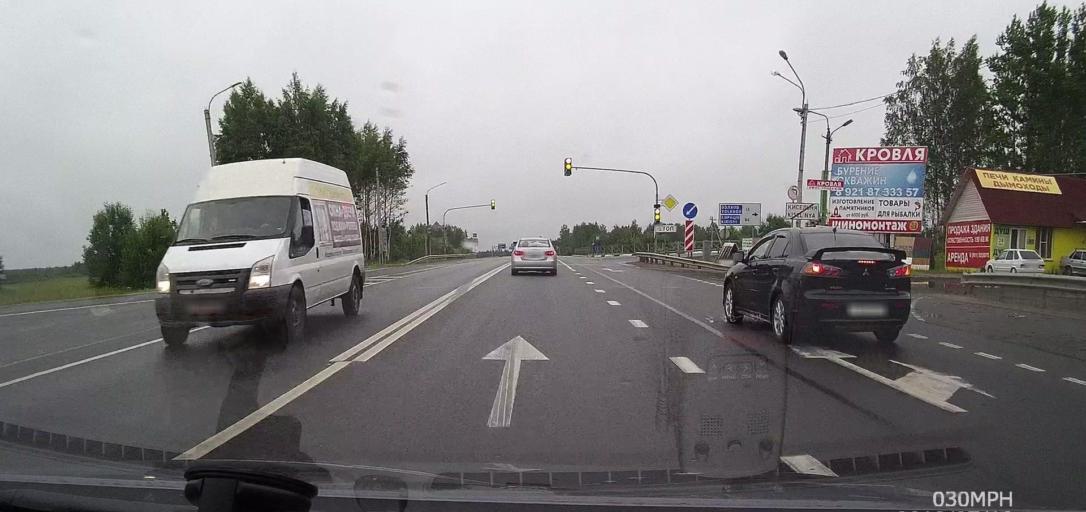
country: RU
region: Leningrad
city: Staraya Ladoga
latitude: 60.0111
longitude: 32.1523
